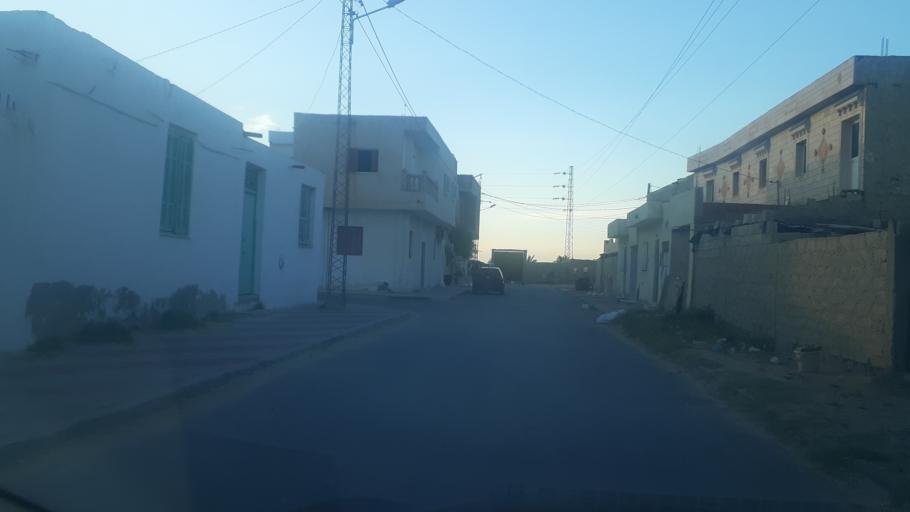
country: TN
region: Qabis
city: Gabes
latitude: 33.9328
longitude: 10.0426
